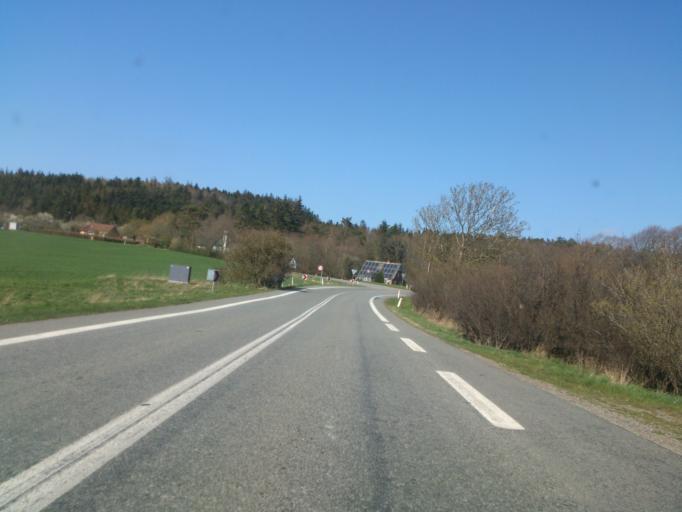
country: DK
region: Central Jutland
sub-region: Favrskov Kommune
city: Ulstrup
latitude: 56.4544
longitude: 9.7506
